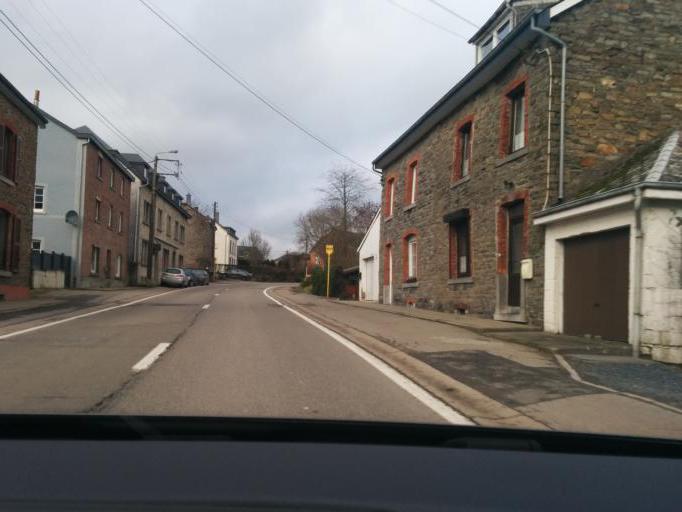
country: BE
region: Wallonia
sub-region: Province du Luxembourg
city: Gouvy
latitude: 50.1899
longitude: 5.9510
